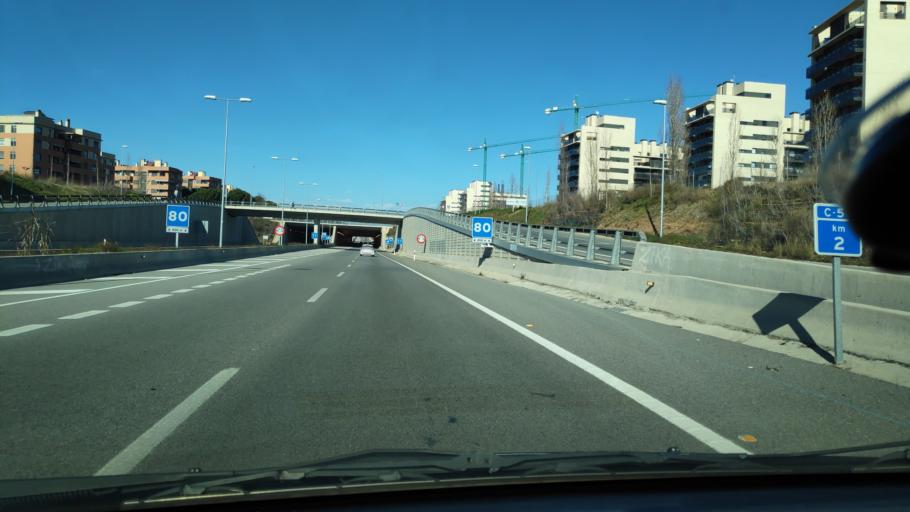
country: ES
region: Catalonia
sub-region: Provincia de Barcelona
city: Sant Quirze del Valles
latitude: 41.5587
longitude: 2.0785
